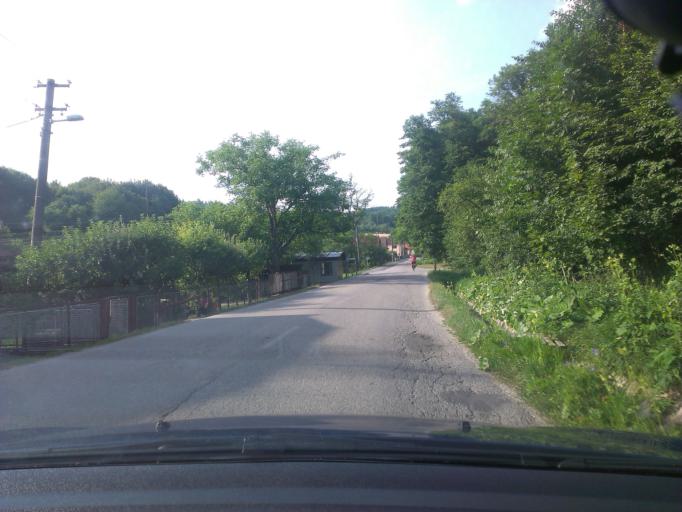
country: SK
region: Trenciansky
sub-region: Okres Myjava
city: Myjava
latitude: 48.8007
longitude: 17.5900
